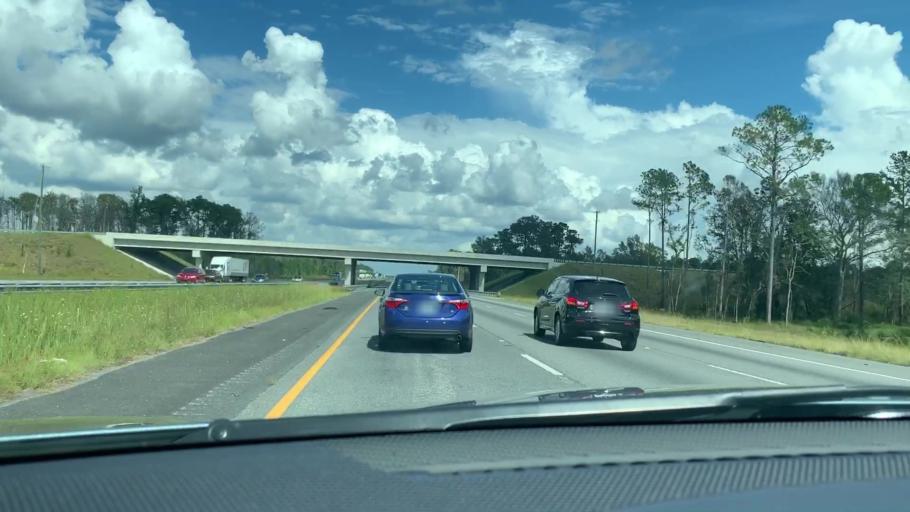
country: US
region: Georgia
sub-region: Camden County
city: Woodbine
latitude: 31.0552
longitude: -81.6403
